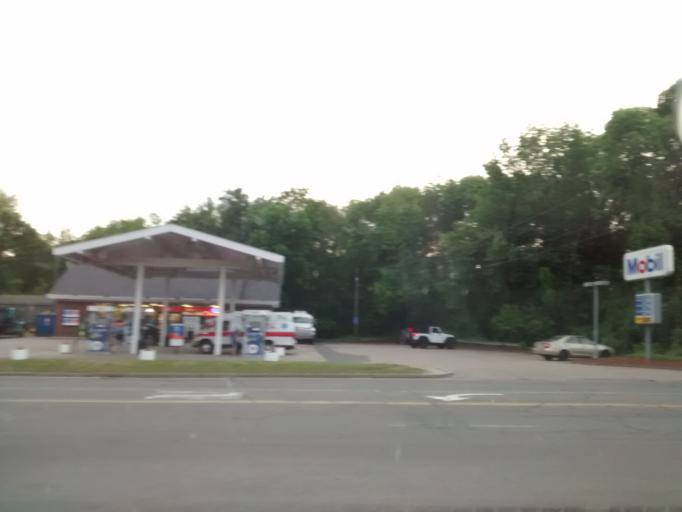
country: US
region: Massachusetts
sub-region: Worcester County
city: Milford
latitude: 42.1636
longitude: -71.5084
